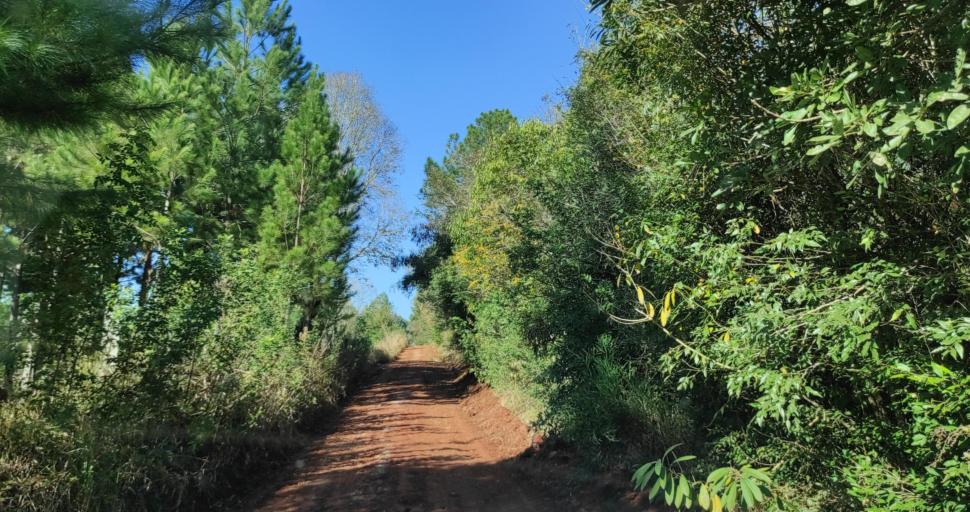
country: AR
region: Misiones
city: Capiovi
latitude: -26.8727
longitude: -55.0363
